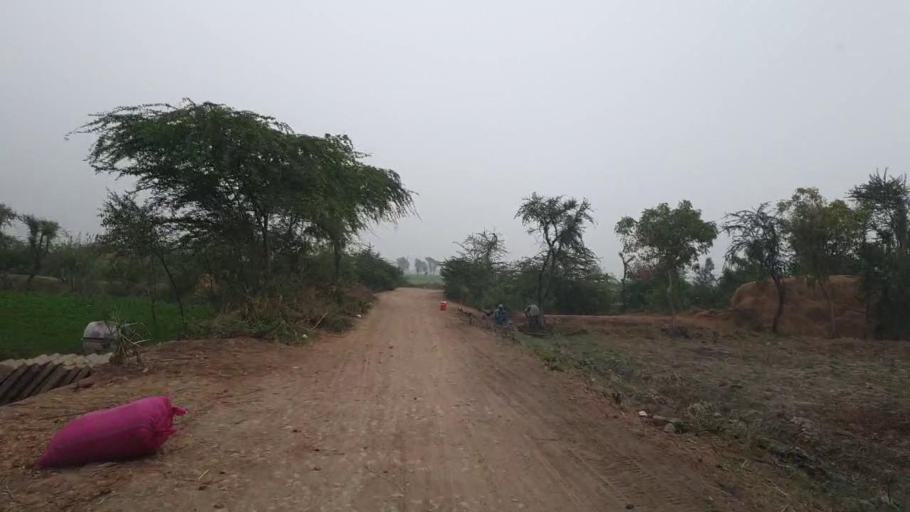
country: PK
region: Sindh
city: Badin
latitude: 24.6269
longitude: 68.7022
